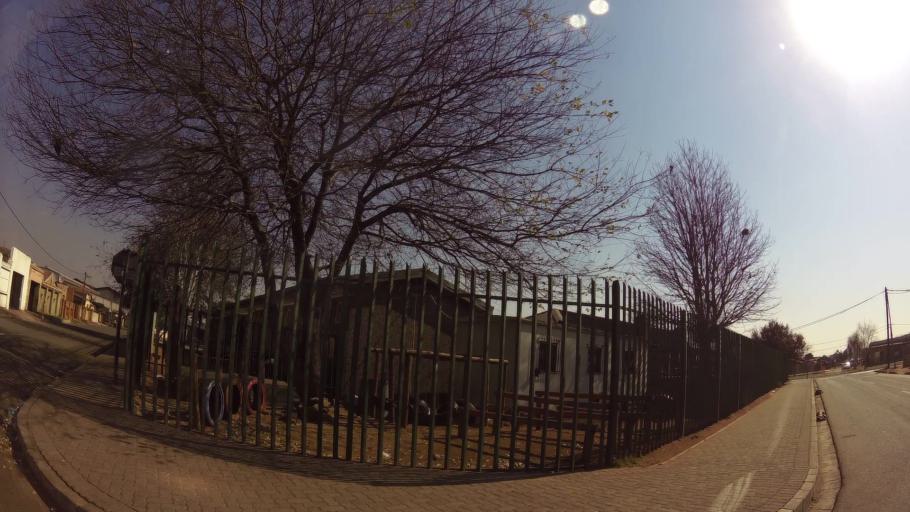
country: ZA
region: Gauteng
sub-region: Ekurhuleni Metropolitan Municipality
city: Boksburg
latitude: -26.2159
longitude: 28.2920
